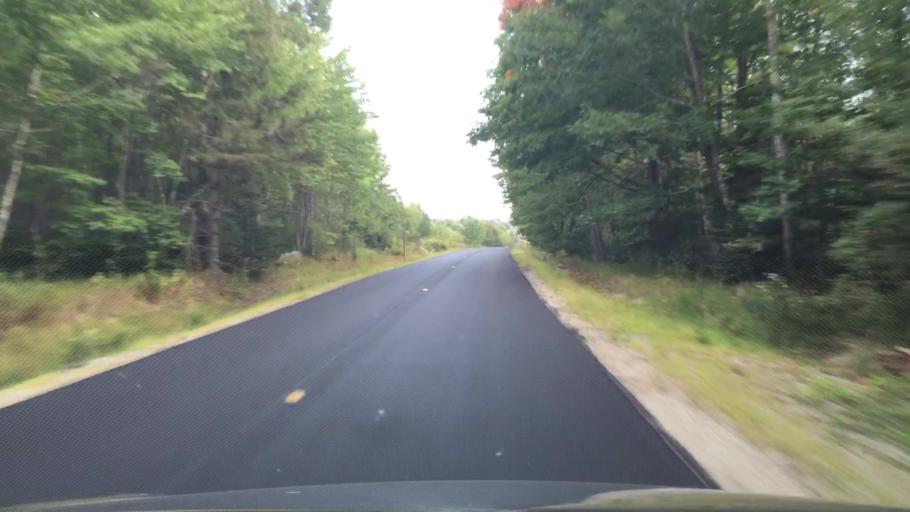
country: US
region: Maine
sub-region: Hancock County
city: Orland
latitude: 44.5426
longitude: -68.6169
